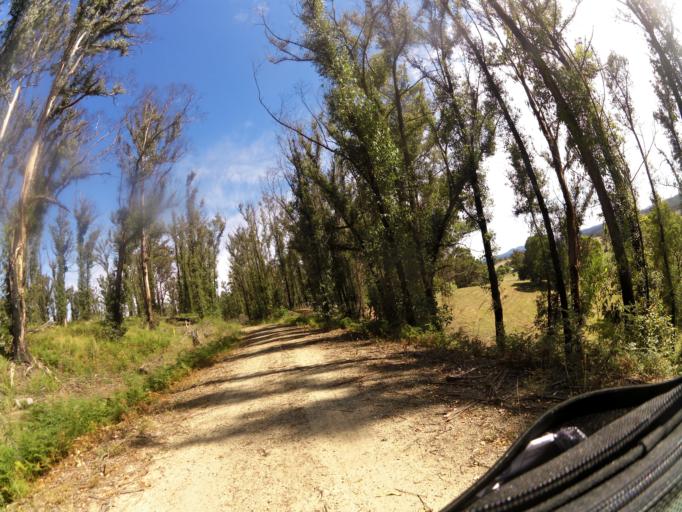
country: AU
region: Victoria
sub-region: East Gippsland
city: Lakes Entrance
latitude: -37.7288
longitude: 148.1627
